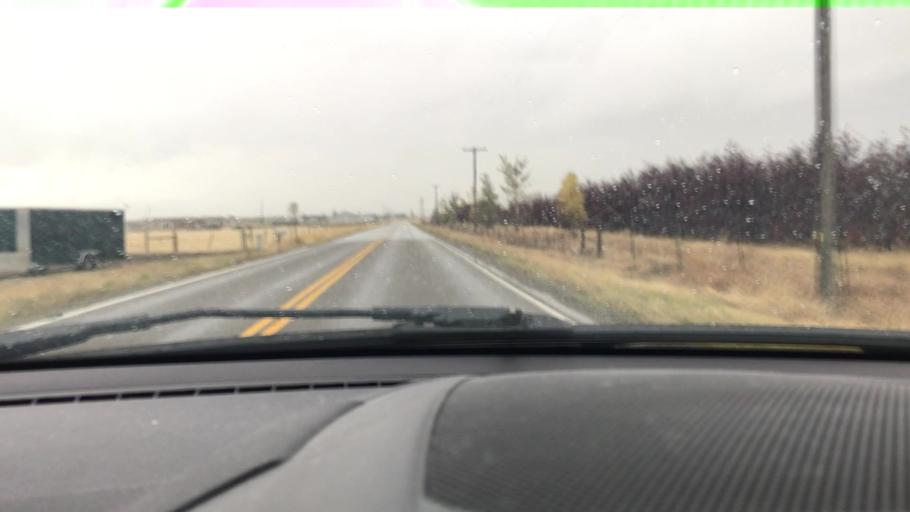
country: US
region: Montana
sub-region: Gallatin County
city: Belgrade
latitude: 45.7506
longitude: -111.1646
